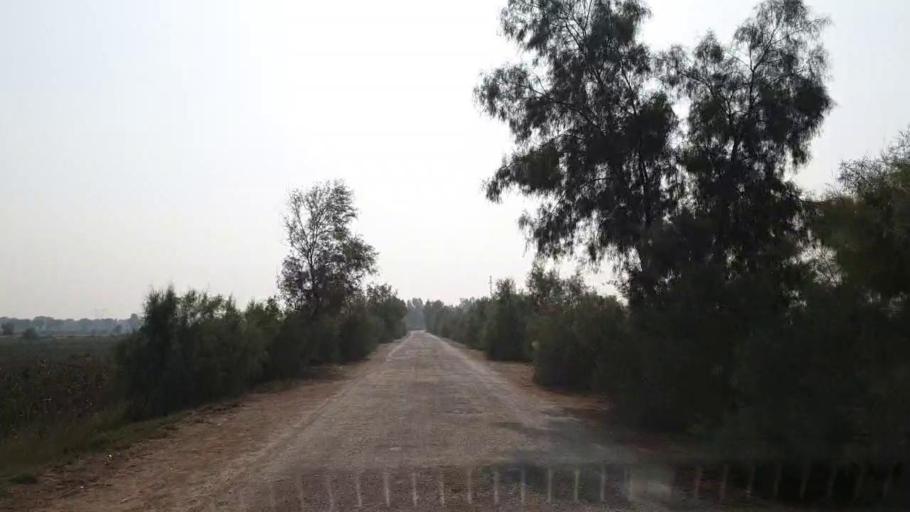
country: PK
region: Sindh
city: Sehwan
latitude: 26.4688
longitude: 67.7766
